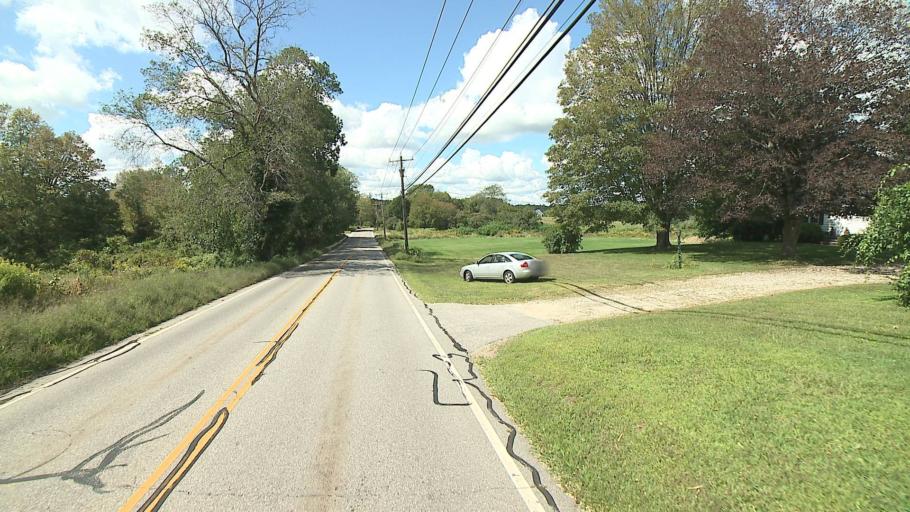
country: US
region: Connecticut
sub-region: Windham County
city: Putnam
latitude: 41.8976
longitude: -71.9322
